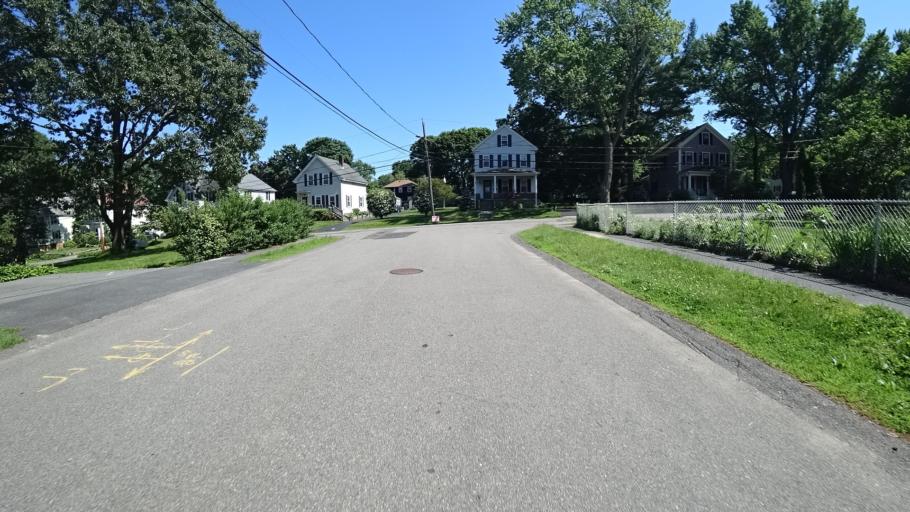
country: US
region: Massachusetts
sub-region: Norfolk County
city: Dedham
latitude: 42.2392
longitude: -71.1524
